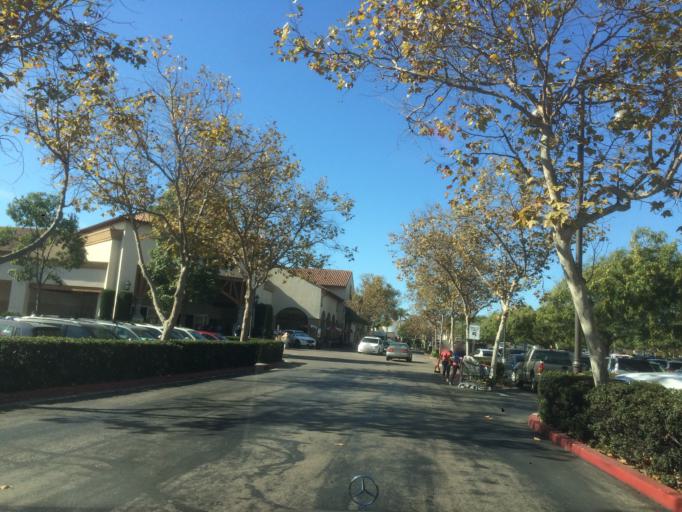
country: US
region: California
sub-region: Santa Barbara County
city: Isla Vista
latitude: 34.4286
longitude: -119.8736
